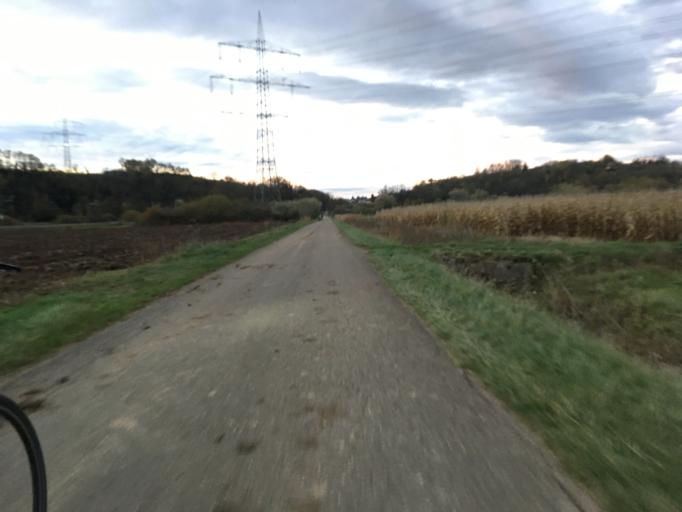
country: DE
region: Baden-Wuerttemberg
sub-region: Freiburg Region
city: Riegel
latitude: 48.1373
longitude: 7.7440
